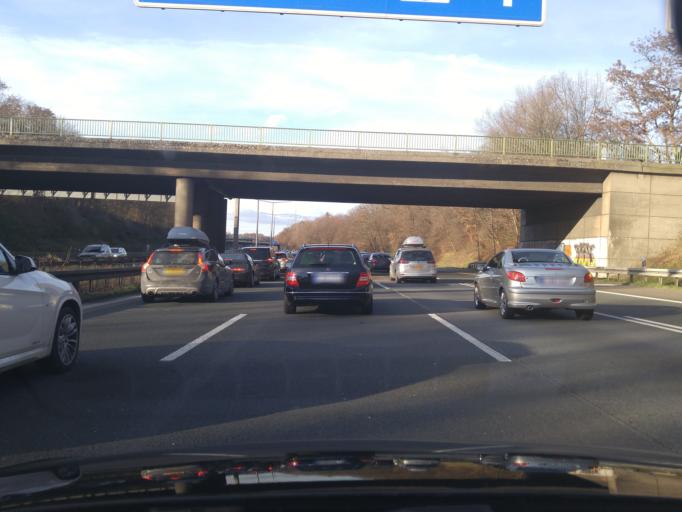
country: DE
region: North Rhine-Westphalia
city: Opladen
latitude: 51.0467
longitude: 7.0037
